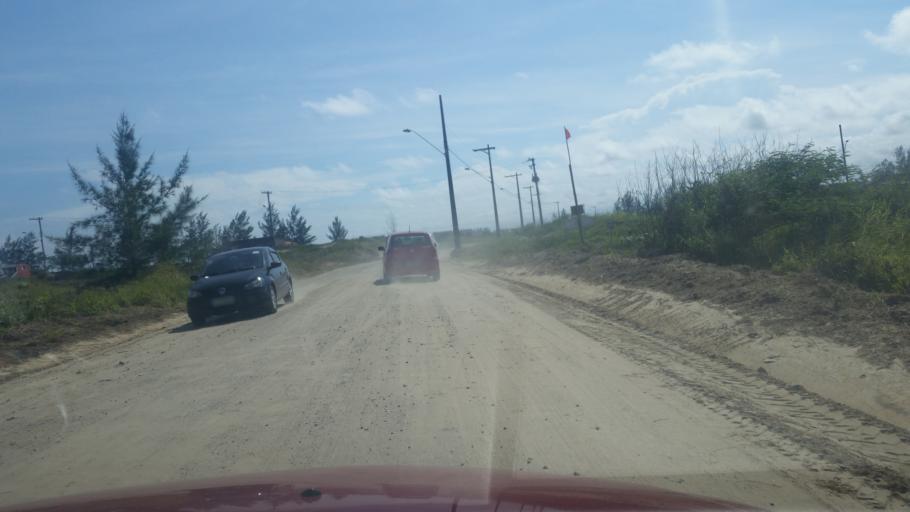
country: BR
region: Sao Paulo
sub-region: Iguape
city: Iguape
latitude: -24.7006
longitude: -47.4616
